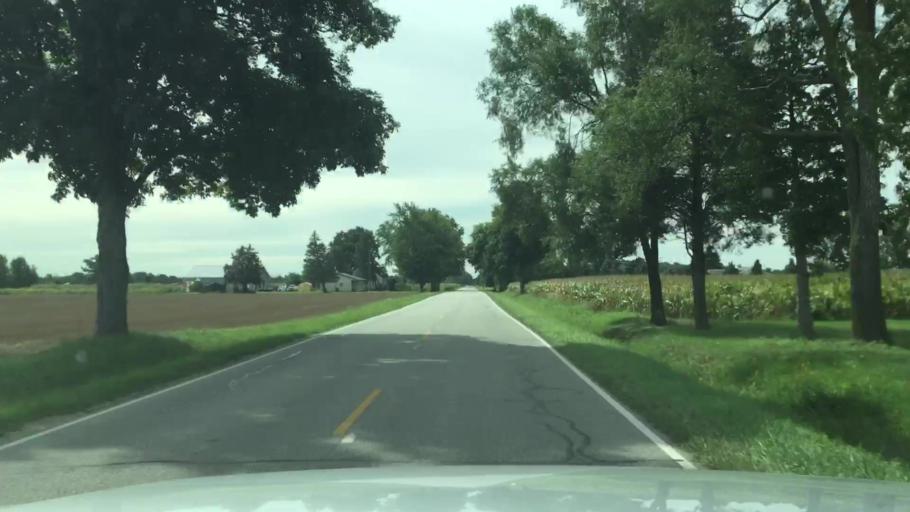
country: US
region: Michigan
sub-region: Genesee County
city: Montrose
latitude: 43.1264
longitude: -83.9880
